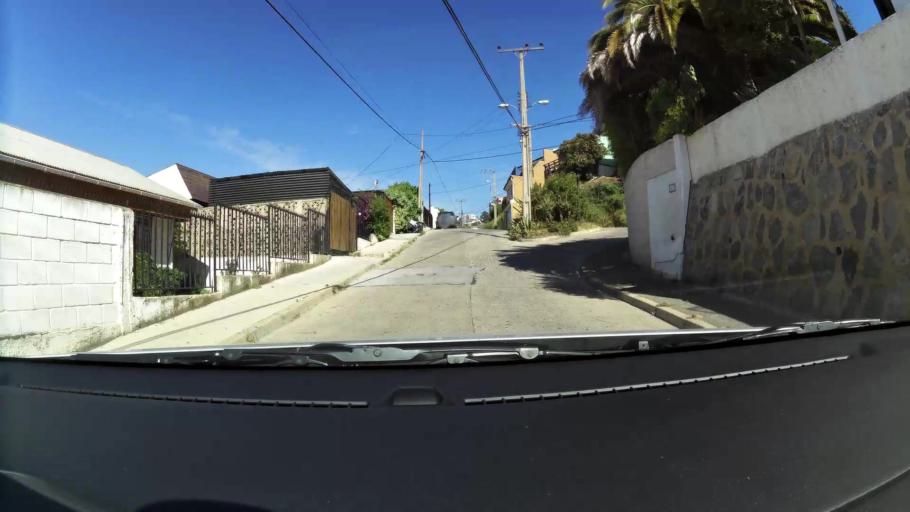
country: CL
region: Valparaiso
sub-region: Provincia de Valparaiso
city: Vina del Mar
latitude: -33.0344
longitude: -71.5657
